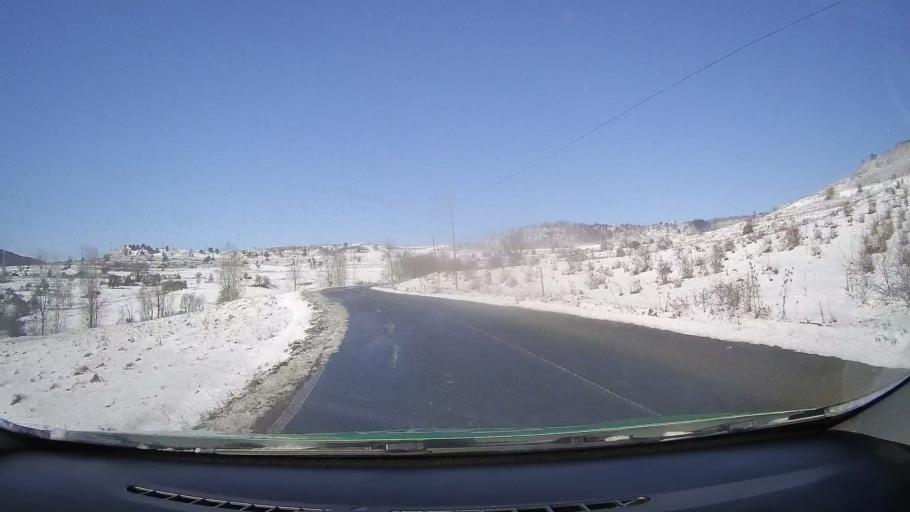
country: RO
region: Sibiu
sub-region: Comuna Avrig
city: Avrig
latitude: 45.7725
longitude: 24.3836
